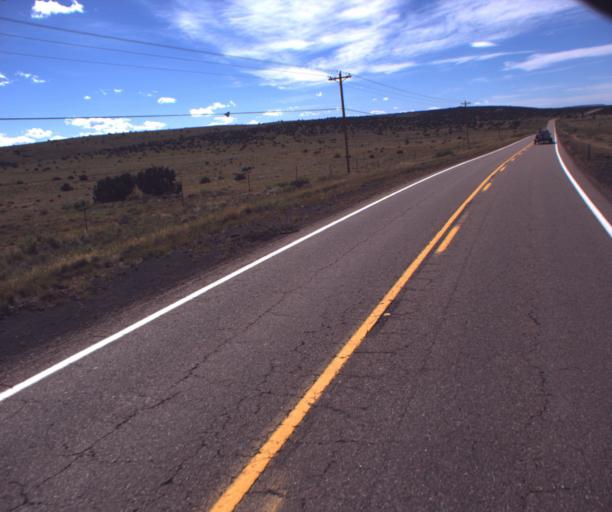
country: US
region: Arizona
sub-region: Apache County
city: Saint Johns
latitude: 34.4881
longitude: -109.5275
